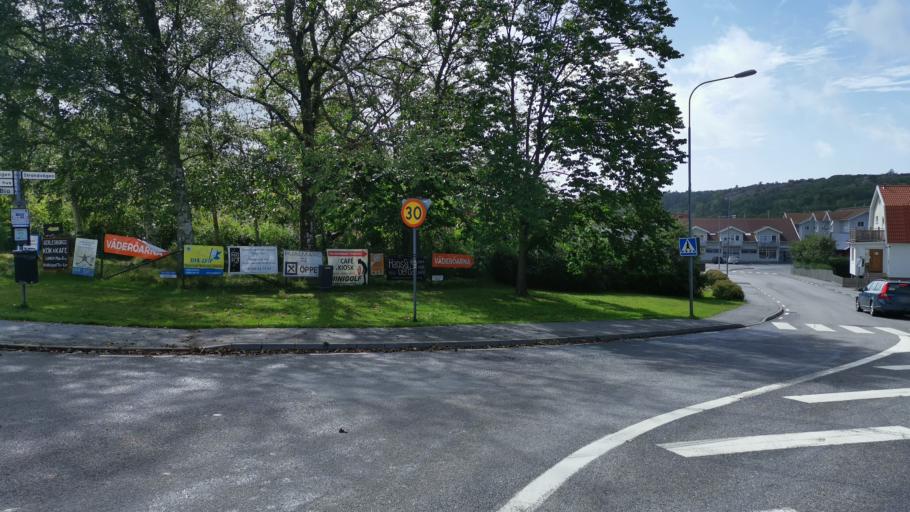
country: SE
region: Vaestra Goetaland
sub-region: Sotenas Kommun
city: Hunnebostrand
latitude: 58.5535
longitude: 11.2743
